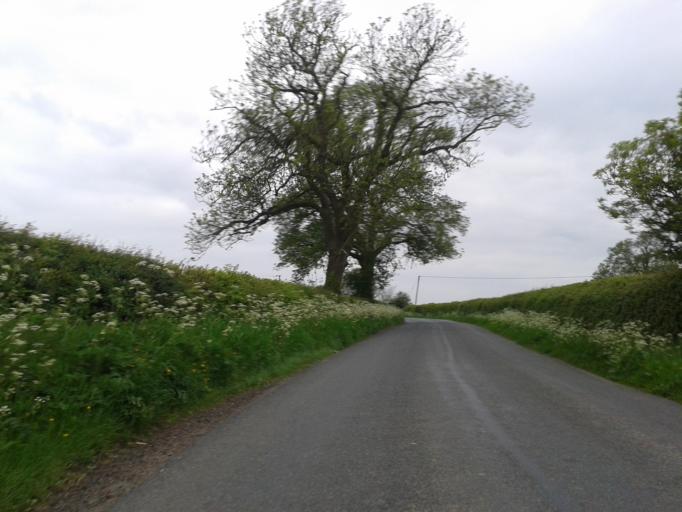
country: GB
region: England
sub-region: Leicestershire
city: Countesthorpe
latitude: 52.5142
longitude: -1.1156
